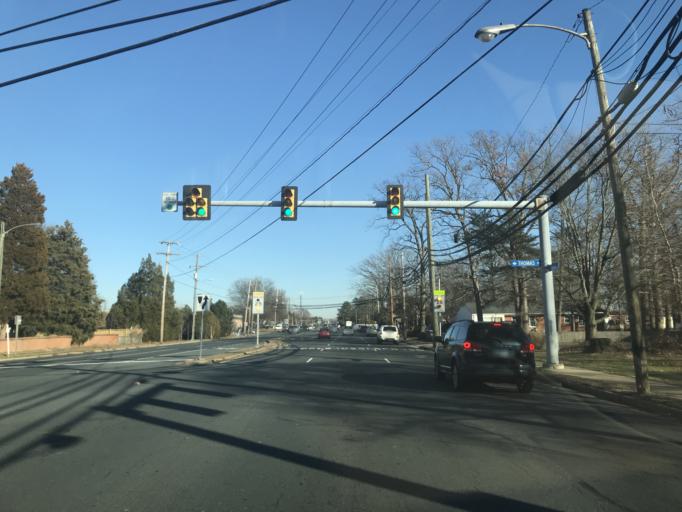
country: US
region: Virginia
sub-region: Fairfax County
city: Franconia
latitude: 38.7786
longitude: -77.1639
